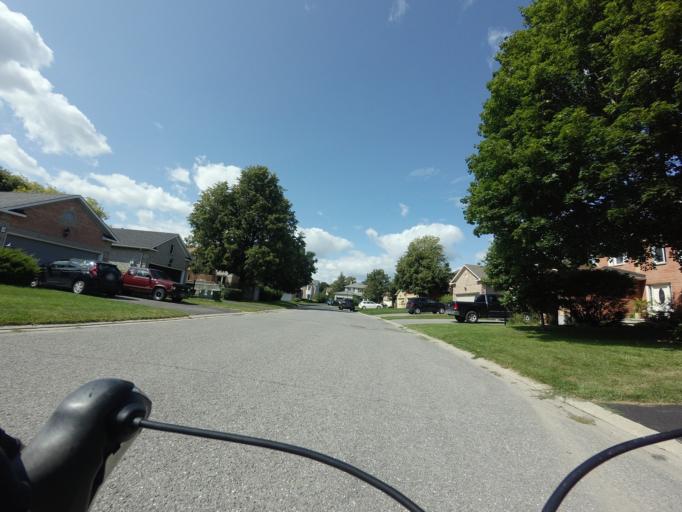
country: CA
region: Ontario
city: Bells Corners
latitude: 45.2903
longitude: -75.8672
